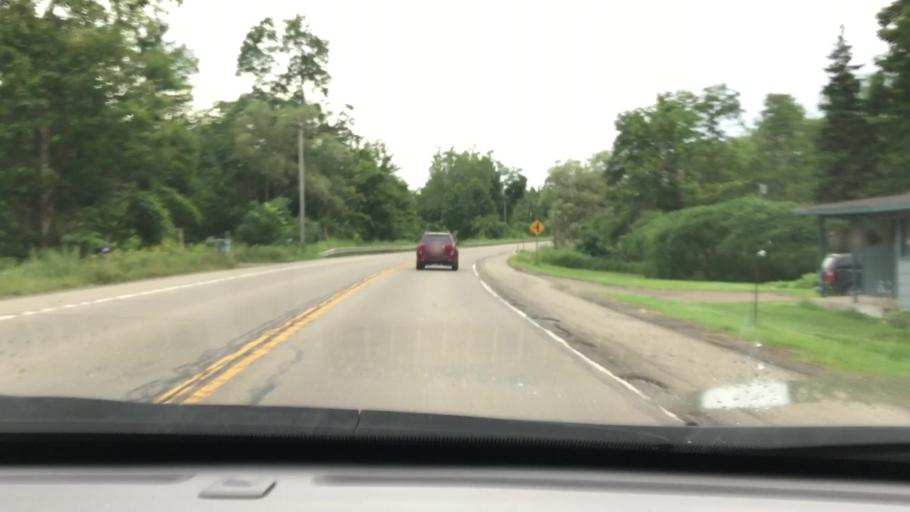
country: US
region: New York
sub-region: Erie County
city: Springville
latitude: 42.4172
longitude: -78.6932
